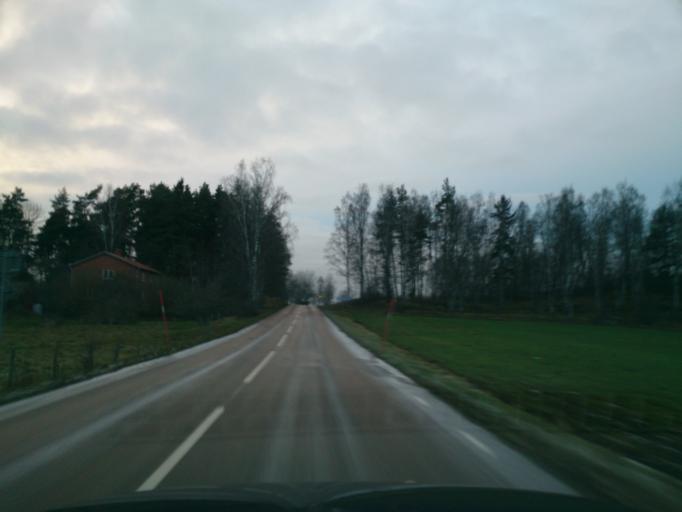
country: SE
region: OEstergoetland
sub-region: Norrkopings Kommun
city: Kimstad
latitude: 58.4247
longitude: 15.9096
